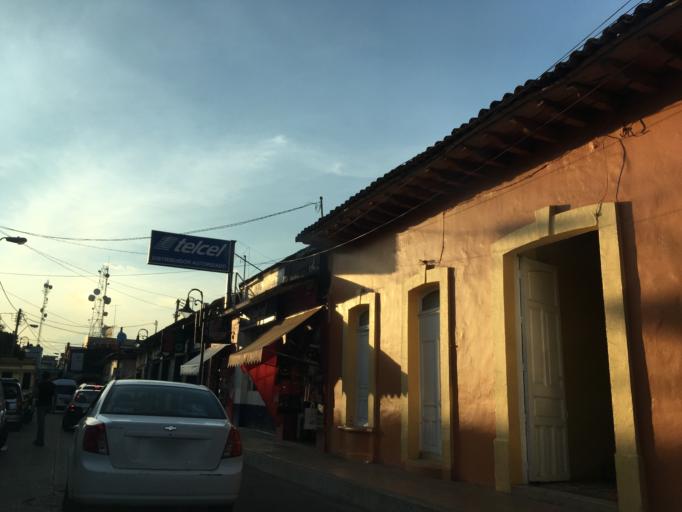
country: MX
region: Michoacan
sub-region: Los Reyes
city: La Higuerita (Colonia San Rafael)
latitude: 19.5894
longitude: -102.4730
